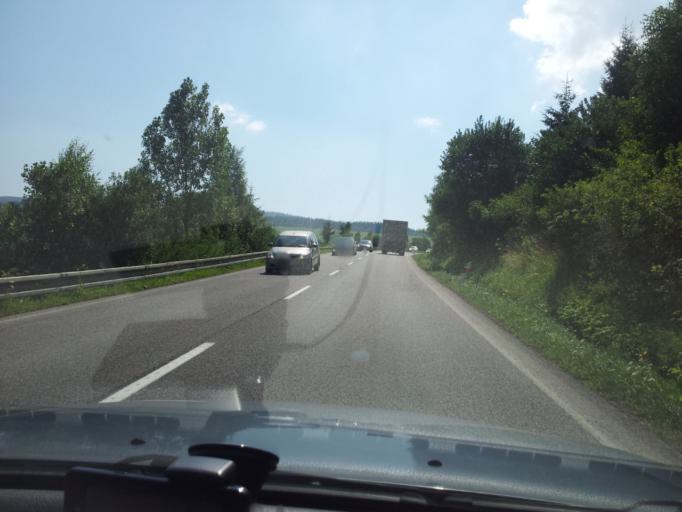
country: SK
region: Zilinsky
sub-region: Okres Dolny Kubin
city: Dolny Kubin
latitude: 49.3093
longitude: 19.3512
